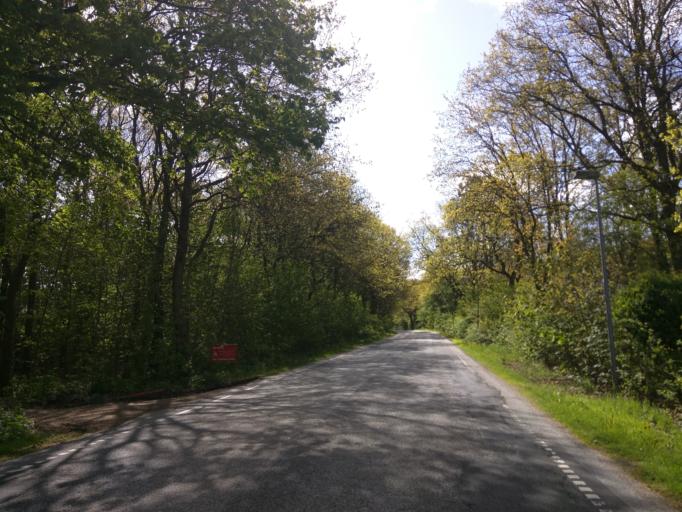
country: DK
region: Central Jutland
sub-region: Viborg Kommune
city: Viborg
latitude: 56.4091
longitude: 9.4221
